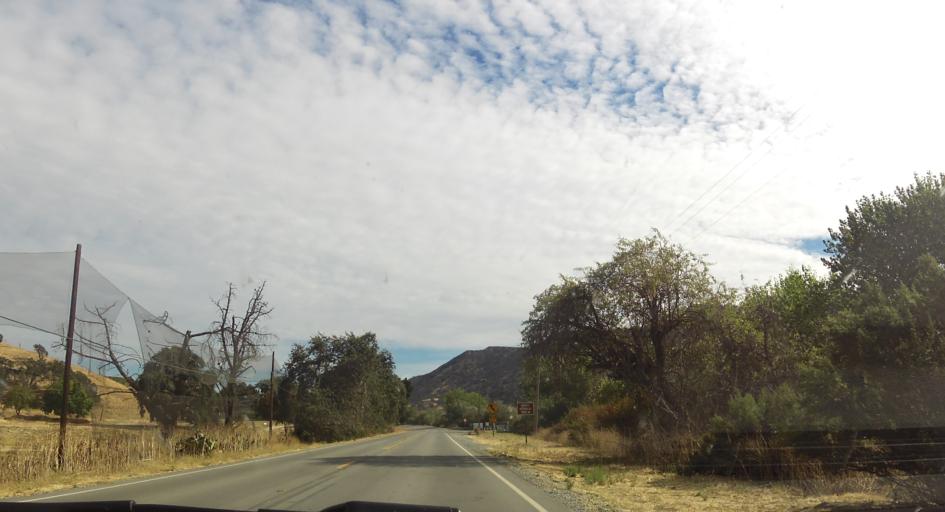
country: US
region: California
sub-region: San Benito County
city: Ridgemark
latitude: 36.7751
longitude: -121.3101
